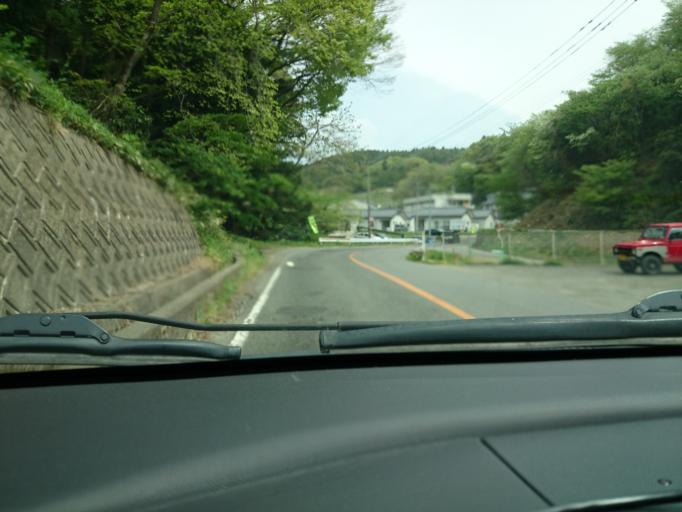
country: JP
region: Fukushima
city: Nihommatsu
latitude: 37.5929
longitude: 140.4245
